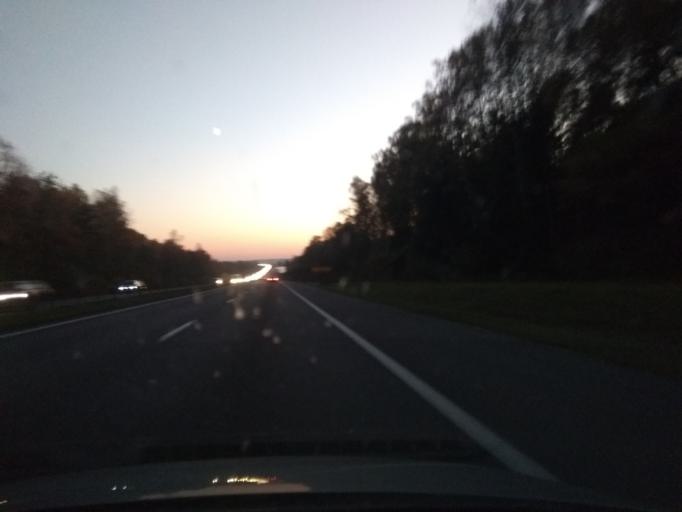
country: BY
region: Minsk
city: Enyerhyetykaw
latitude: 53.6339
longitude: 27.0618
